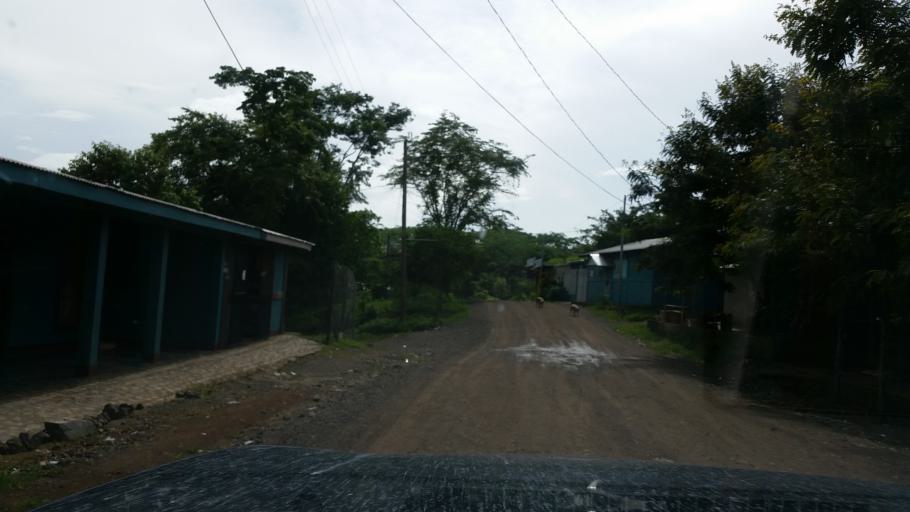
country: NI
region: Atlantico Norte (RAAN)
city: Siuna
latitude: 13.7160
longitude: -84.7708
